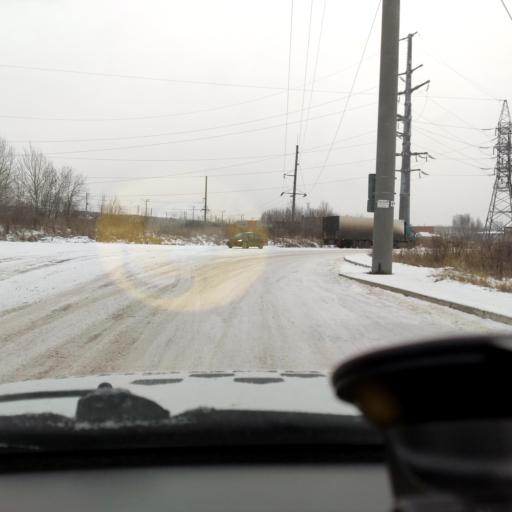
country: RU
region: Perm
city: Kondratovo
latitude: 58.0076
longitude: 56.1500
